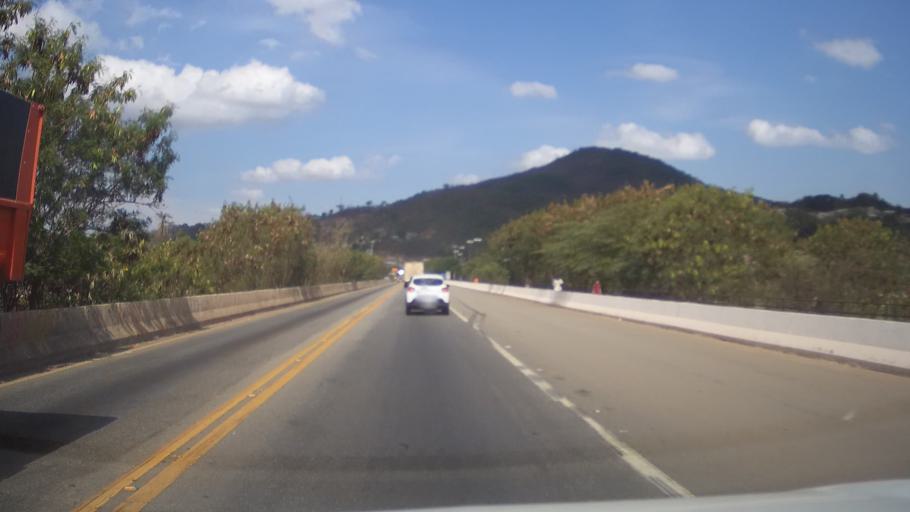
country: BR
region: Minas Gerais
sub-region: Santa Luzia
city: Santa Luzia
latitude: -19.8423
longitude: -43.8687
